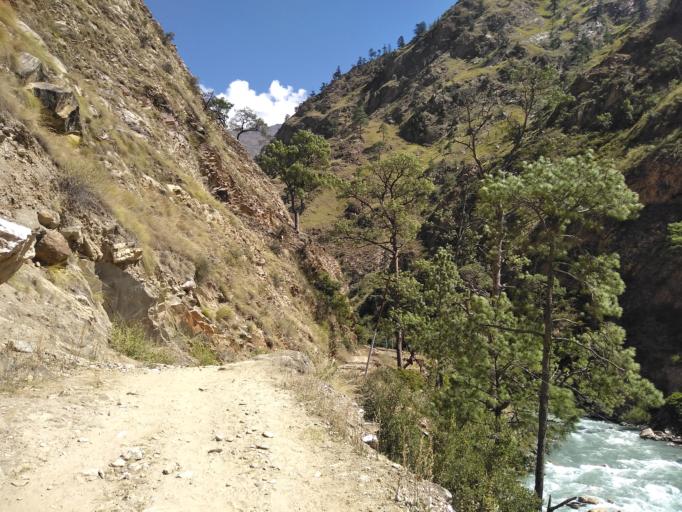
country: NP
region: Western Region
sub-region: Dhawalagiri Zone
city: Jomsom
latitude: 28.9371
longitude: 82.9314
